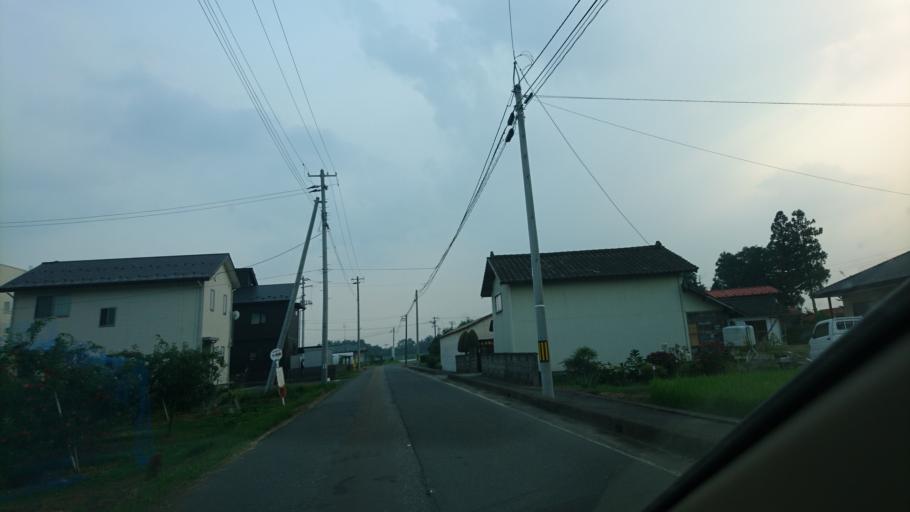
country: JP
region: Iwate
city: Mizusawa
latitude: 39.1702
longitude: 141.1685
